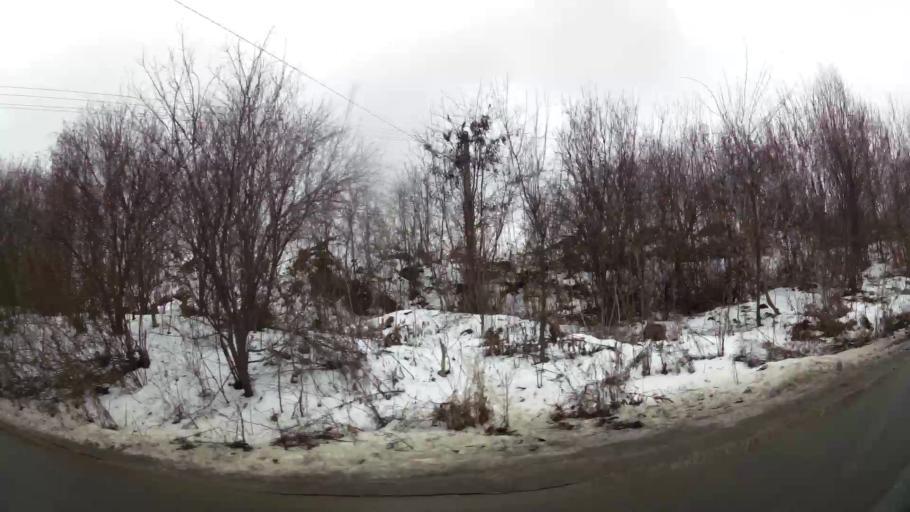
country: RO
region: Ilfov
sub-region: Comuna Chitila
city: Chitila
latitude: 44.4990
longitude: 26.0067
